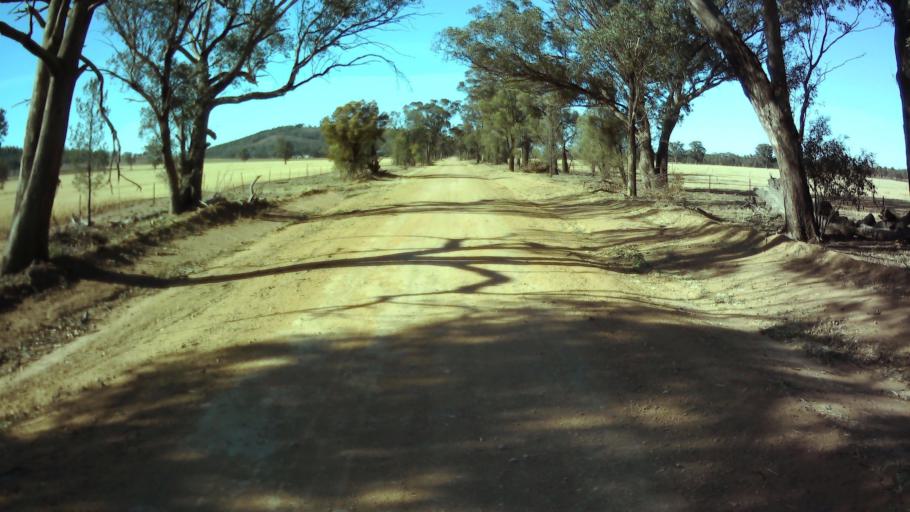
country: AU
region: New South Wales
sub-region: Weddin
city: Grenfell
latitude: -33.8046
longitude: 147.8784
